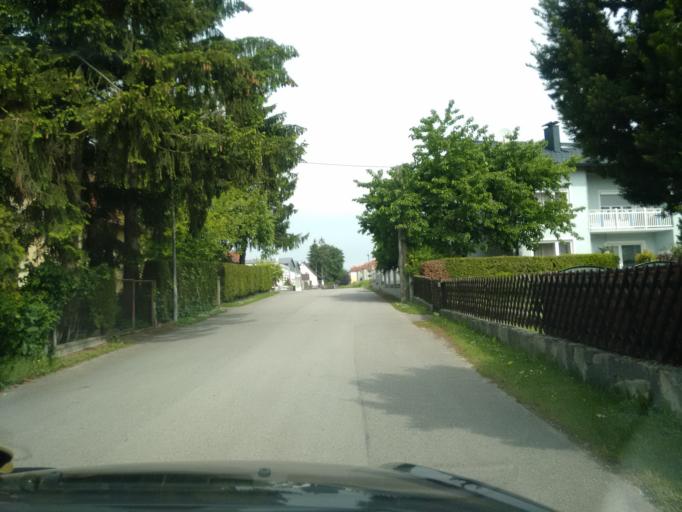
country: AT
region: Upper Austria
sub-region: Politischer Bezirk Linz-Land
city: Traun
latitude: 48.2254
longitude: 14.2458
